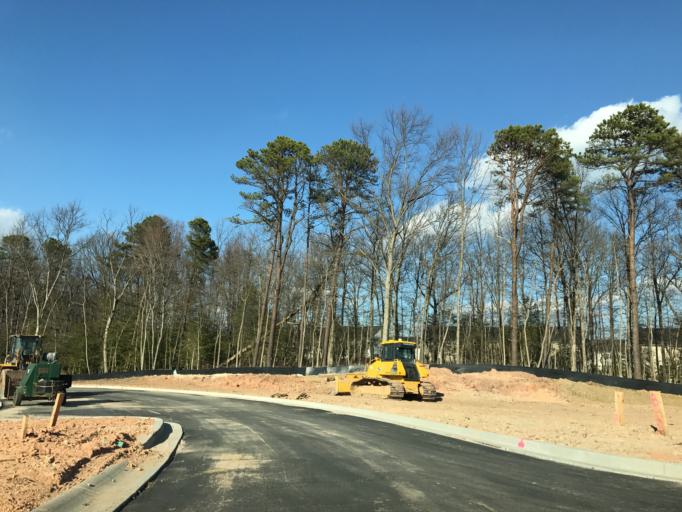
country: US
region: Maryland
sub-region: Anne Arundel County
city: Green Haven
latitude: 39.1673
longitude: -76.5669
